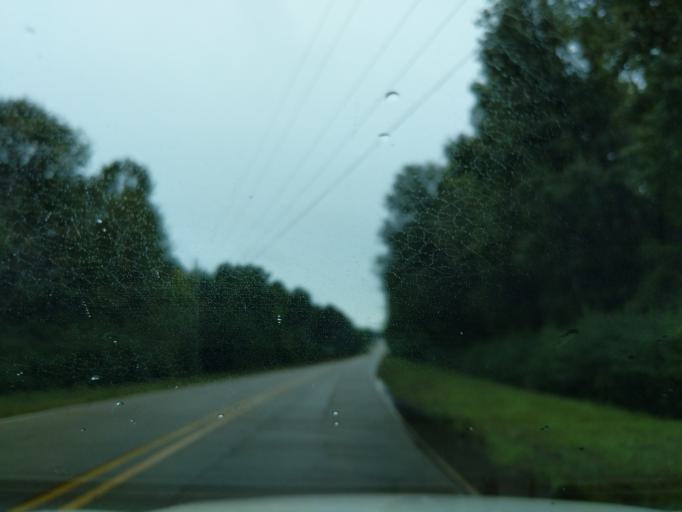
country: US
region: Louisiana
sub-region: Bienville Parish
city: Arcadia
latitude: 32.5554
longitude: -93.0541
